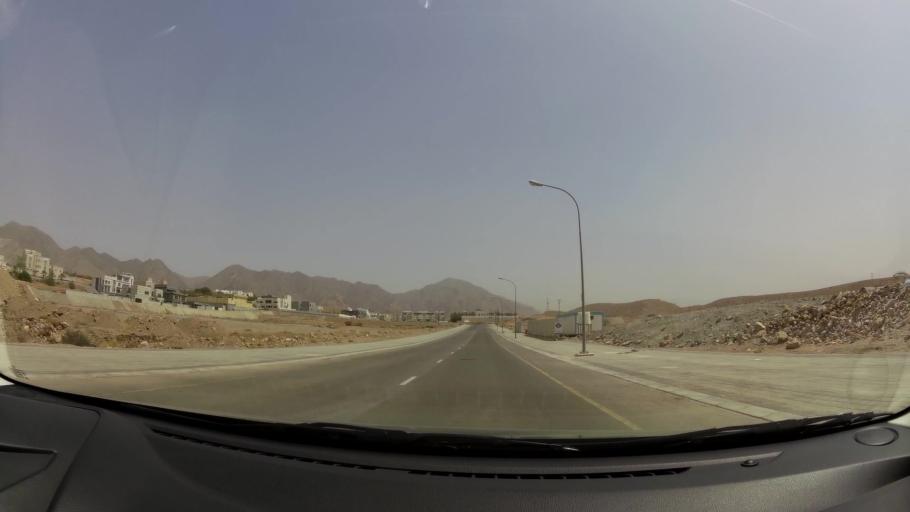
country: OM
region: Muhafazat Masqat
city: Bawshar
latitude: 23.5556
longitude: 58.3931
